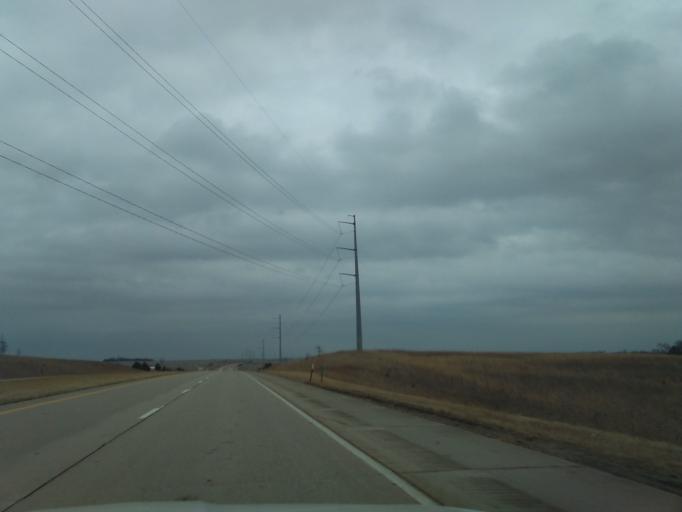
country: US
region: Nebraska
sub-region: Otoe County
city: Syracuse
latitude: 40.6706
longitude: -96.1016
